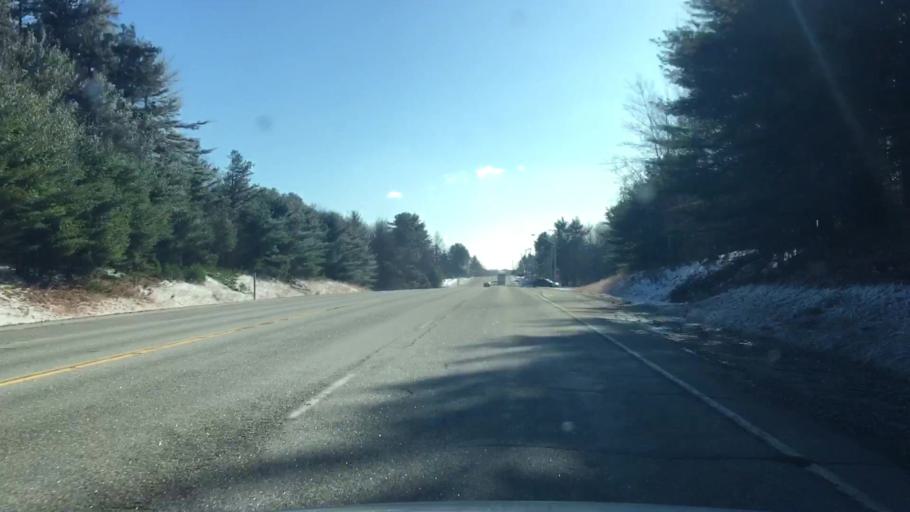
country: US
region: Maine
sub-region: Androscoggin County
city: Lewiston
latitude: 44.1755
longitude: -70.2319
